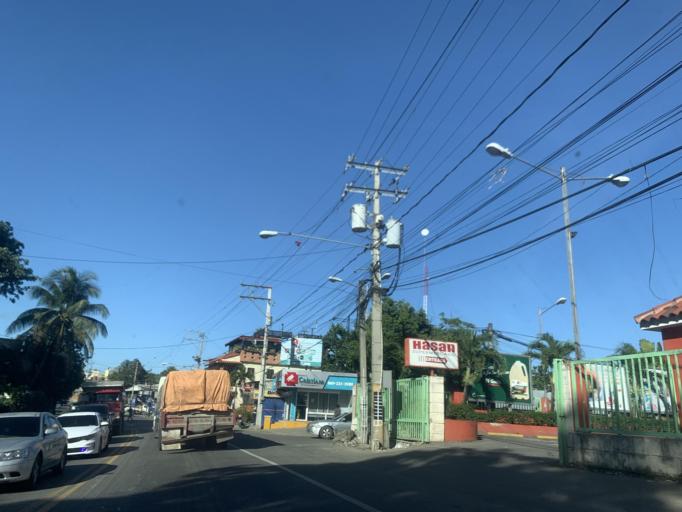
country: DO
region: San Cristobal
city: Bajos de Haina
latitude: 18.4292
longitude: -70.0295
